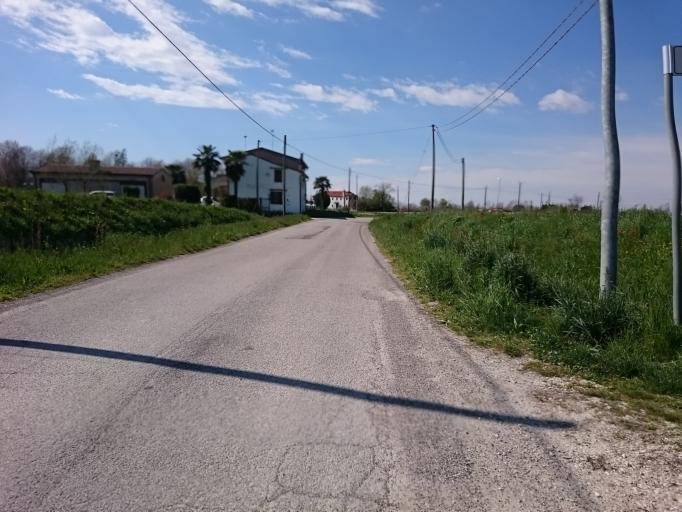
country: IT
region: Veneto
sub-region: Provincia di Padova
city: Brugine
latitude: 45.3043
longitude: 11.9848
